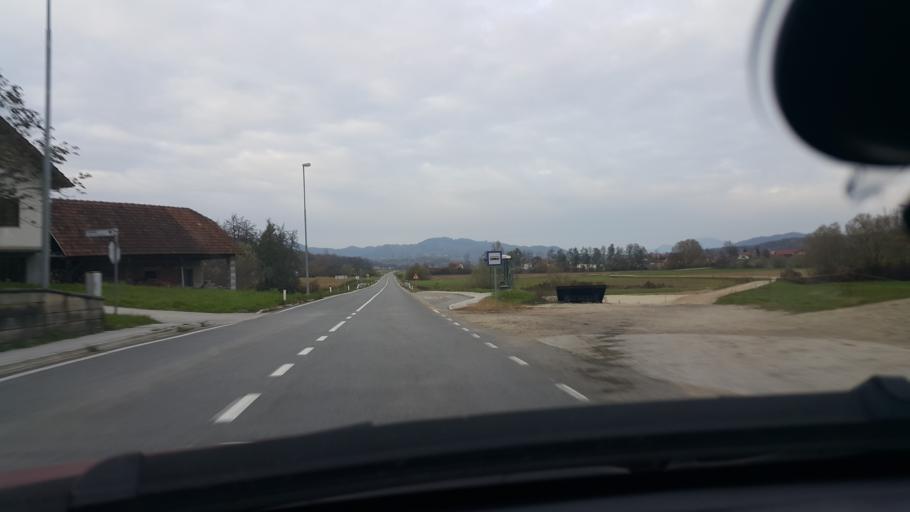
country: SI
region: Bistrica ob Sotli
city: Bistrica ob Sotli
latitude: 46.0905
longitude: 15.6182
